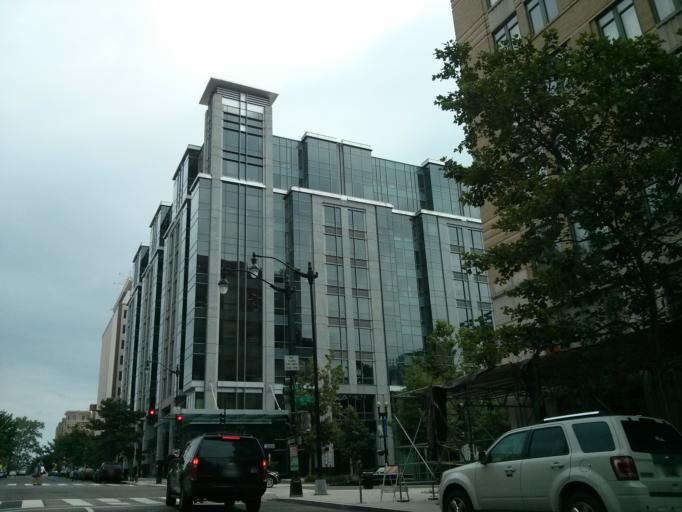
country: US
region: Washington, D.C.
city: Washington, D.C.
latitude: 38.9020
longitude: -77.0281
